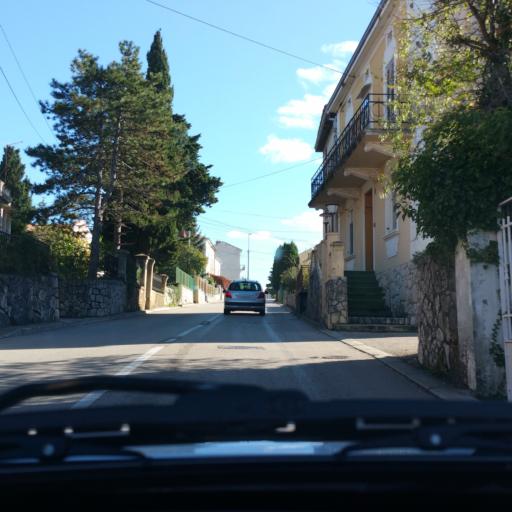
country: HR
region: Primorsko-Goranska
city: Omisalj
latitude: 45.2105
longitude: 14.5567
